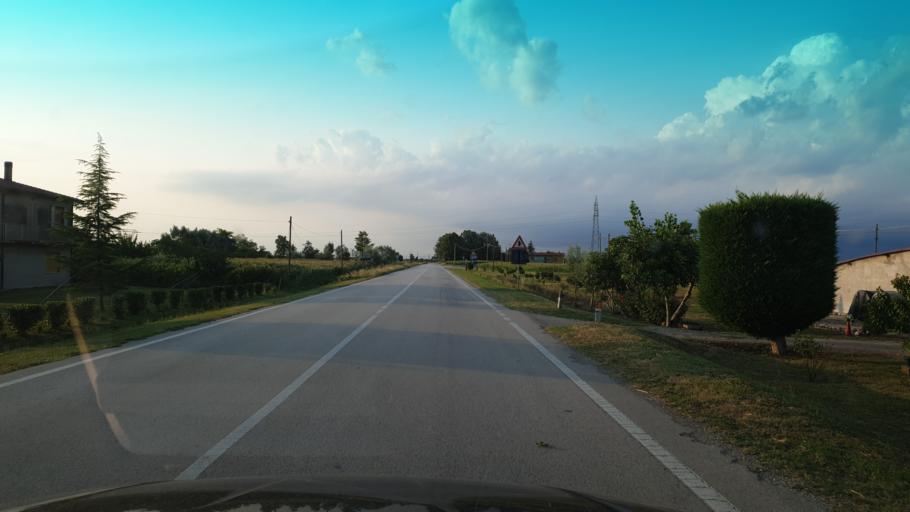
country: IT
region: Veneto
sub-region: Provincia di Rovigo
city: San Bellino
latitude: 45.0467
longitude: 11.5818
